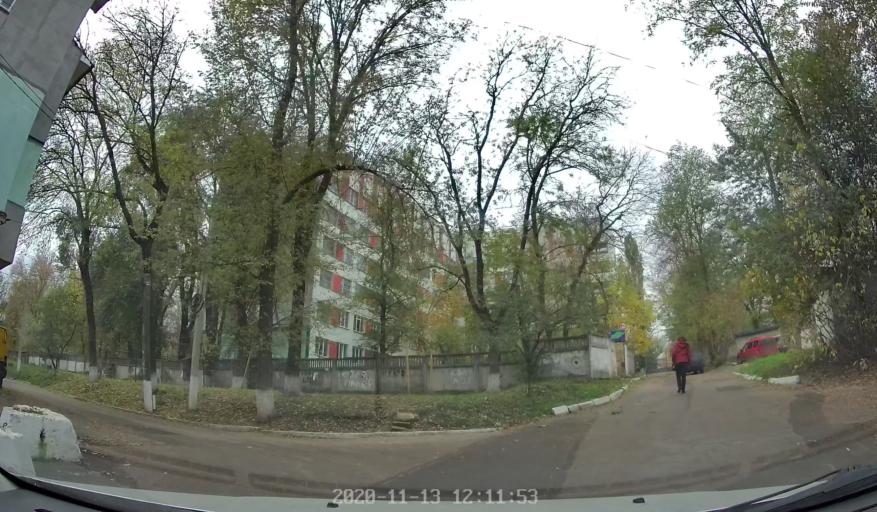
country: MD
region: Chisinau
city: Chisinau
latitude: 46.9565
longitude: 28.8358
